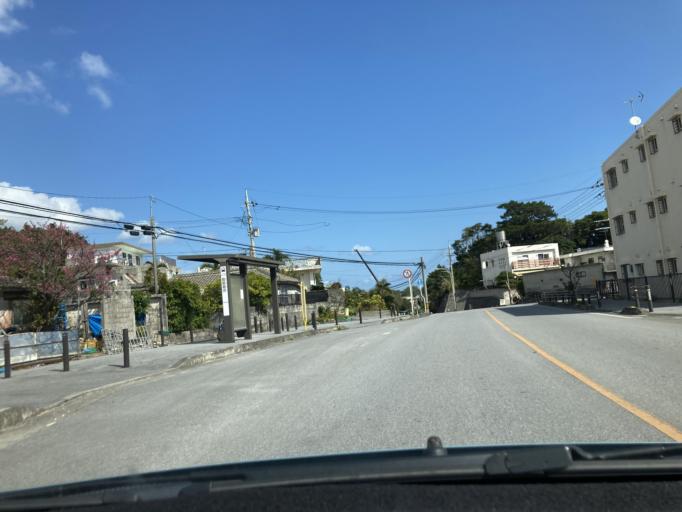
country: JP
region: Okinawa
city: Nago
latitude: 26.6192
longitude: 127.9989
